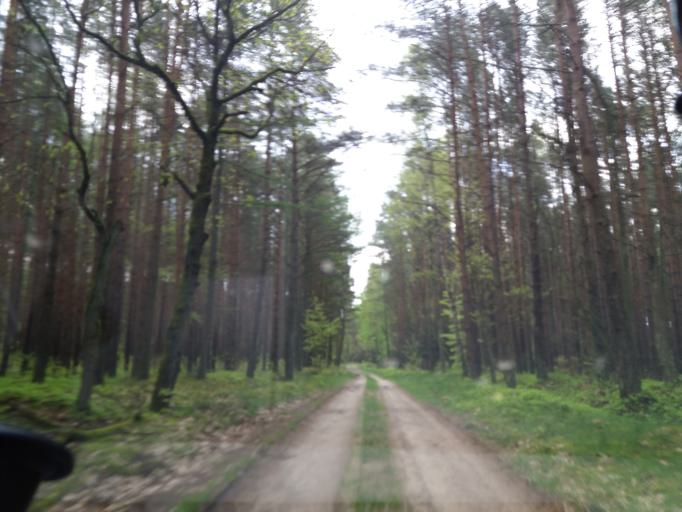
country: PL
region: West Pomeranian Voivodeship
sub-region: Powiat choszczenski
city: Drawno
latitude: 53.1124
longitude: 15.8706
